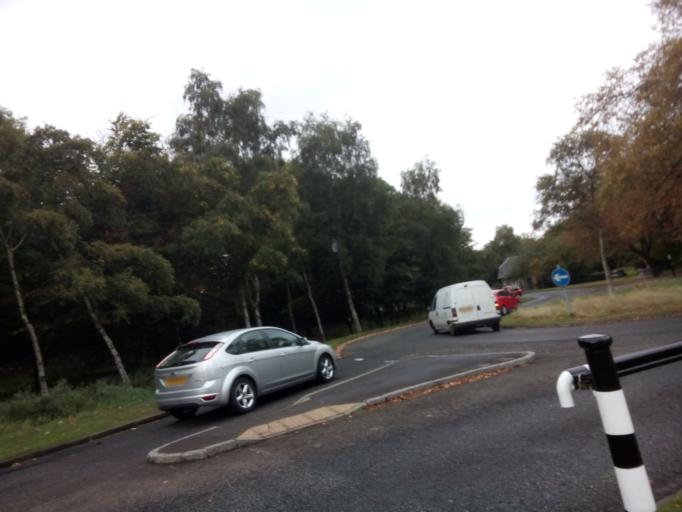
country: GB
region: Scotland
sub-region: Edinburgh
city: Edinburgh
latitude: 55.9414
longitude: -3.1702
